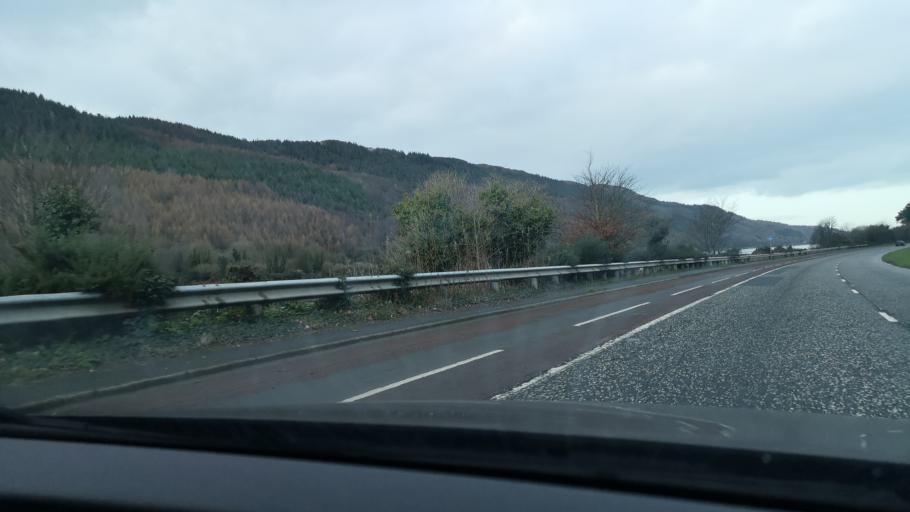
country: GB
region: Northern Ireland
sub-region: Down District
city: Warrenpoint
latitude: 54.1160
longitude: -6.2928
